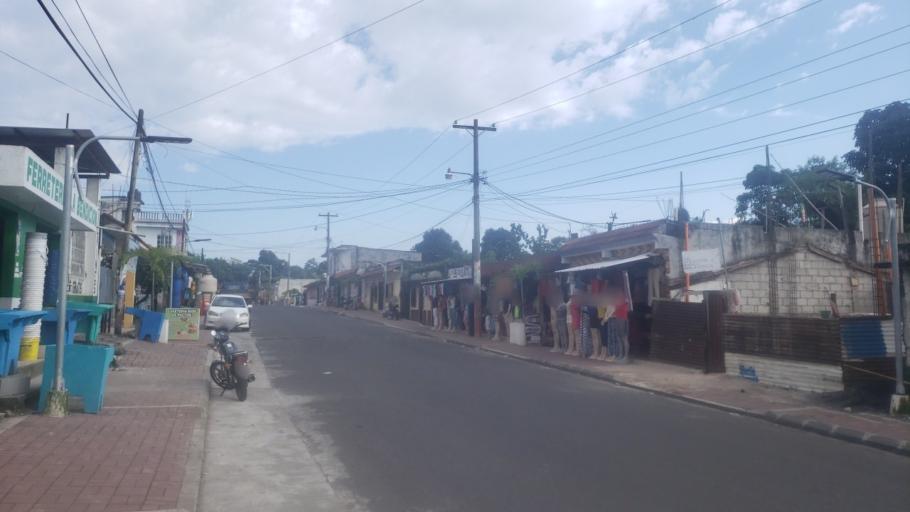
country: GT
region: Quetzaltenango
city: El Palmar
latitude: 14.6451
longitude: -91.5585
